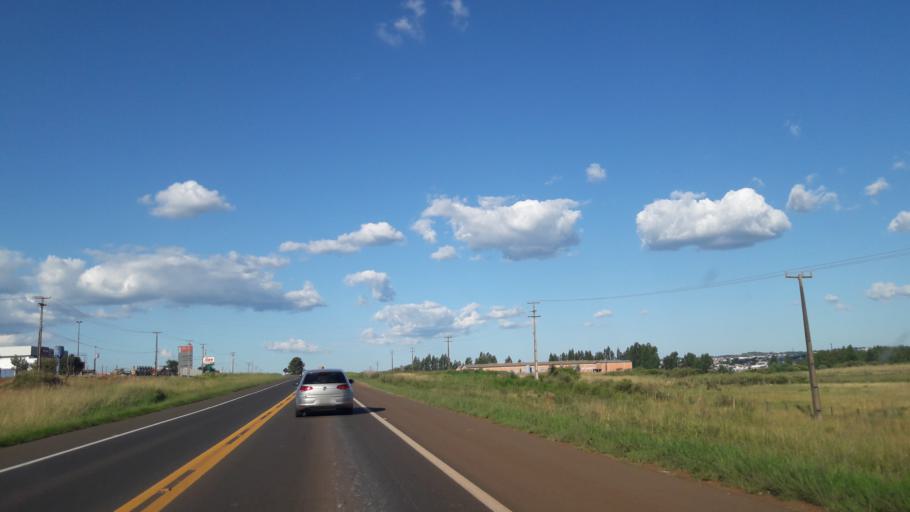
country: BR
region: Parana
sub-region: Guarapuava
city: Guarapuava
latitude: -25.3836
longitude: -51.5122
